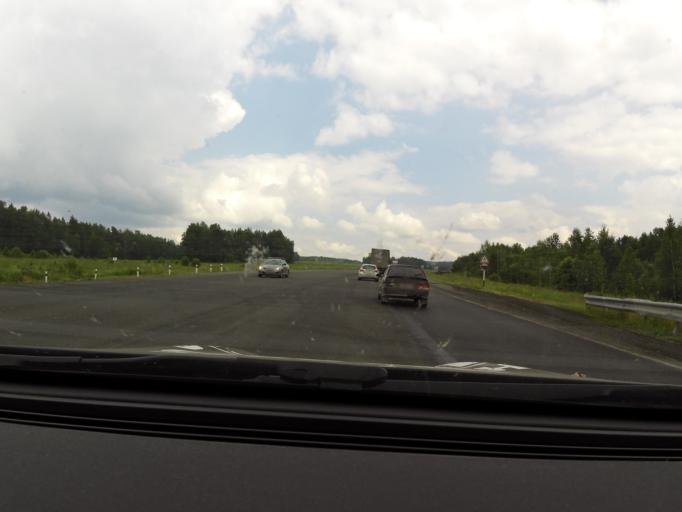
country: RU
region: Sverdlovsk
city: Ufimskiy
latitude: 56.7829
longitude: 58.2704
